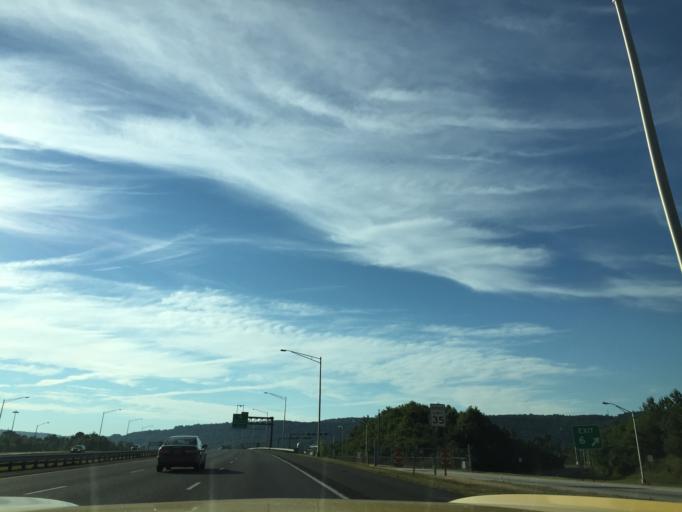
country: US
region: New Jersey
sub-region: Warren County
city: Alpha
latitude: 40.6646
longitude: -75.0907
